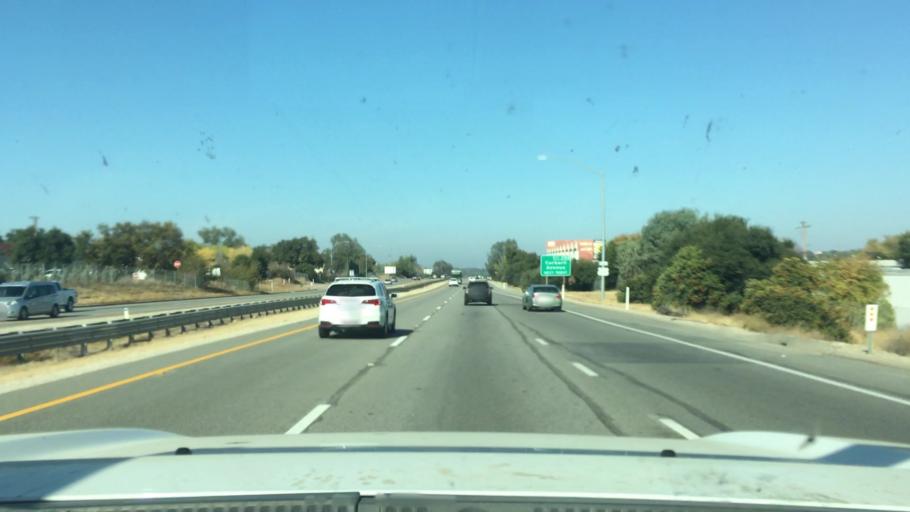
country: US
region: California
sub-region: San Luis Obispo County
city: Atascadero
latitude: 35.4682
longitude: -120.6529
